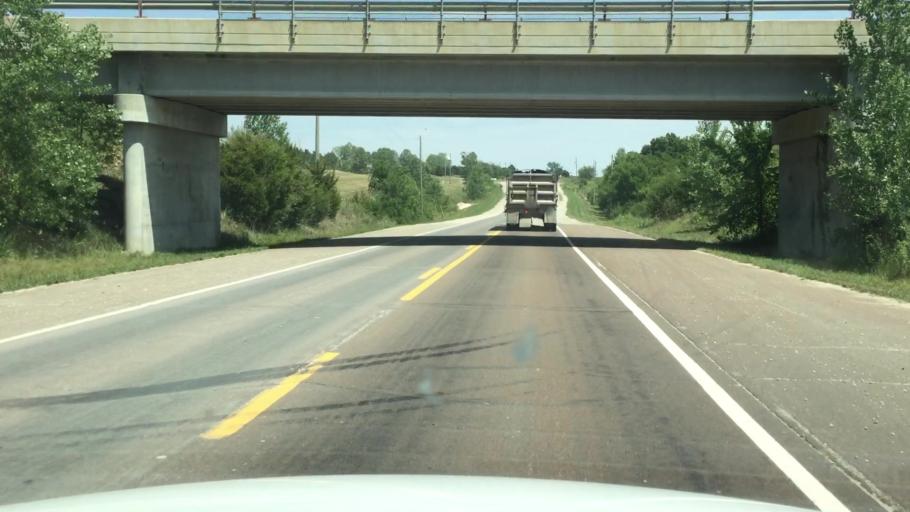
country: US
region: Kansas
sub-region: Shawnee County
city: Topeka
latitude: 38.9859
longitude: -95.5046
